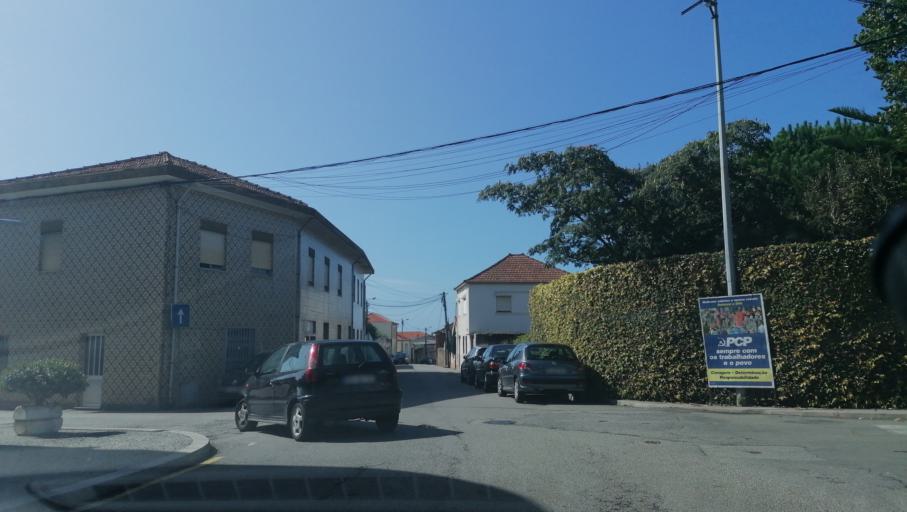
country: PT
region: Aveiro
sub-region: Espinho
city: Silvalde
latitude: 41.0061
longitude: -8.6251
